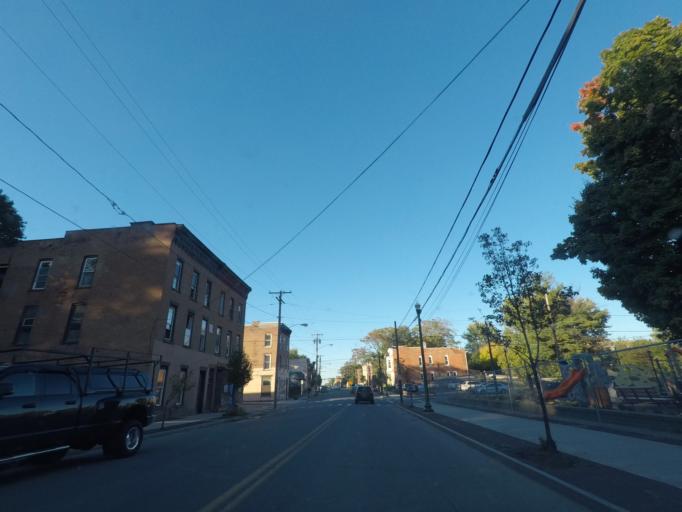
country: US
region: New York
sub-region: Albany County
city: Green Island
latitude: 42.7484
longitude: -73.6826
